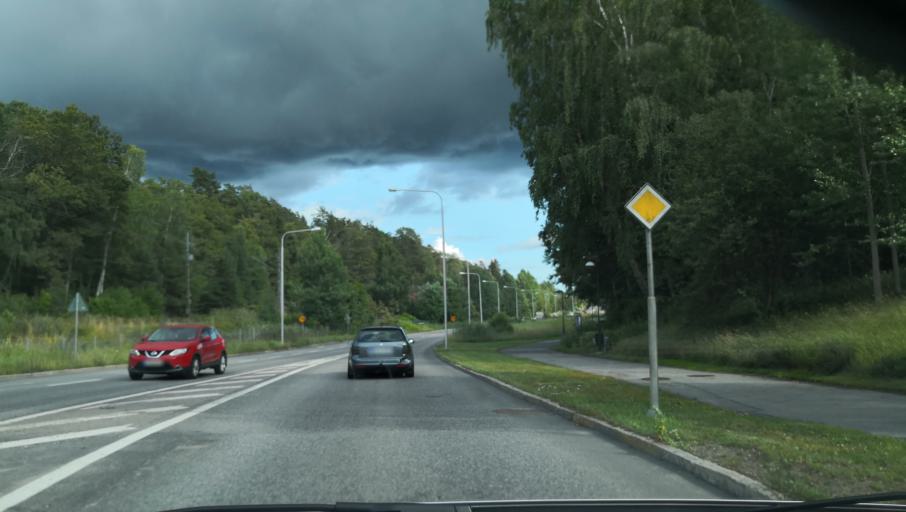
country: SE
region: Stockholm
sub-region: Stockholms Kommun
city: Arsta
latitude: 59.2511
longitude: 18.0600
